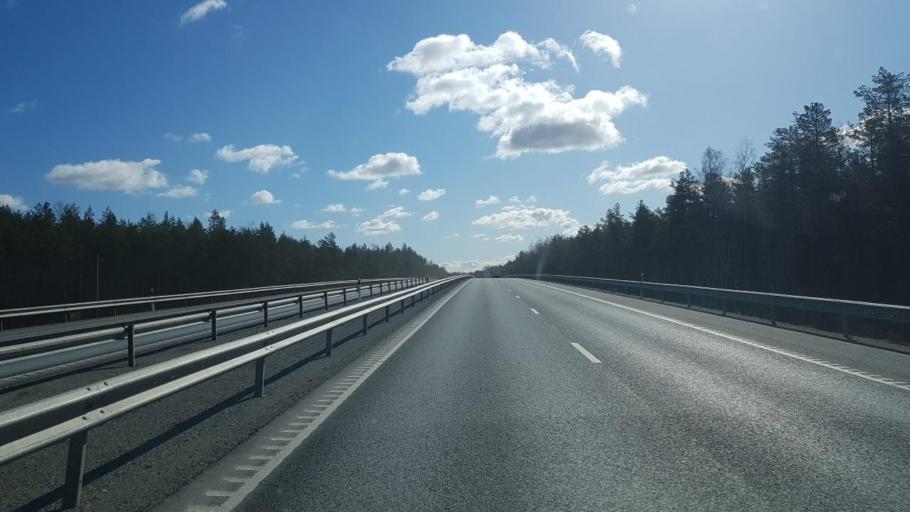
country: EE
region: Harju
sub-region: Saku vald
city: Saku
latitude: 59.3117
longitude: 24.7170
